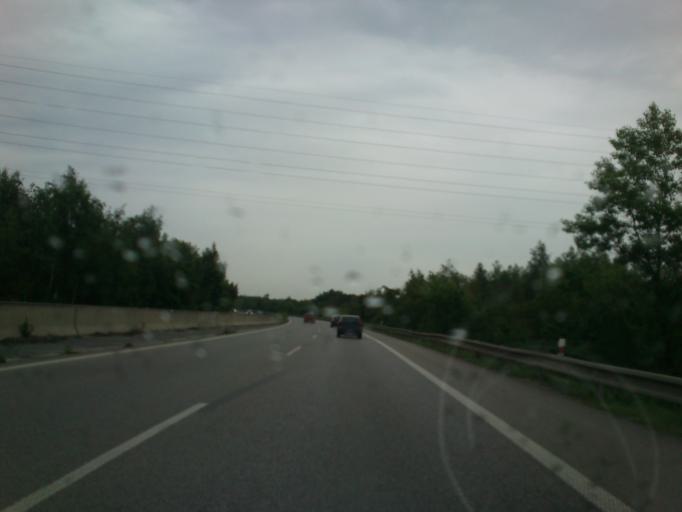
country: CZ
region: Central Bohemia
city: Brandys nad Labem-Stara Boleslav
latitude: 50.1830
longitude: 14.6949
